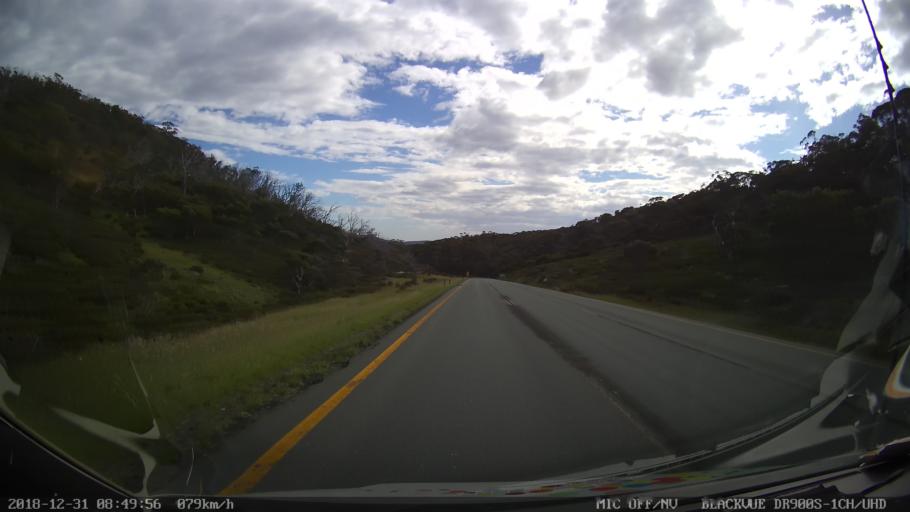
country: AU
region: New South Wales
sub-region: Snowy River
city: Jindabyne
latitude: -36.3575
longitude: 148.5120
